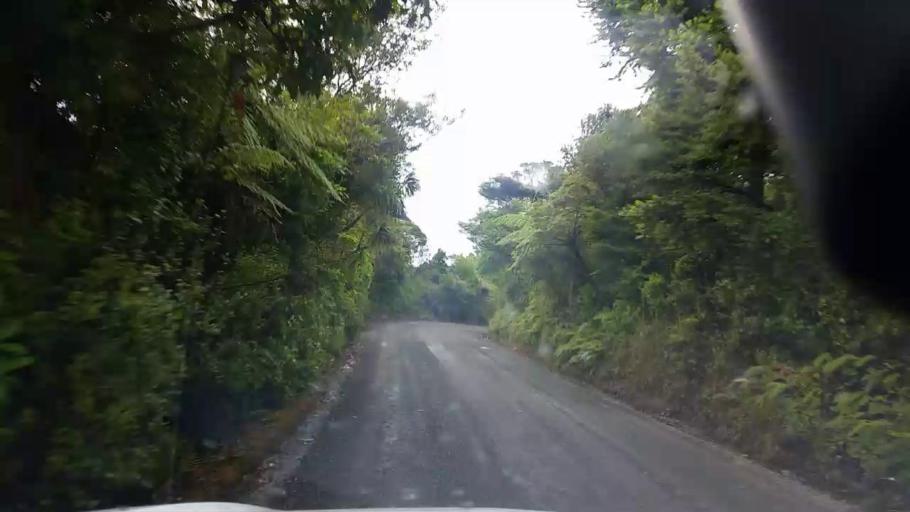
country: NZ
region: Auckland
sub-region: Auckland
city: Muriwai Beach
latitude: -36.9369
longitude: 174.5156
